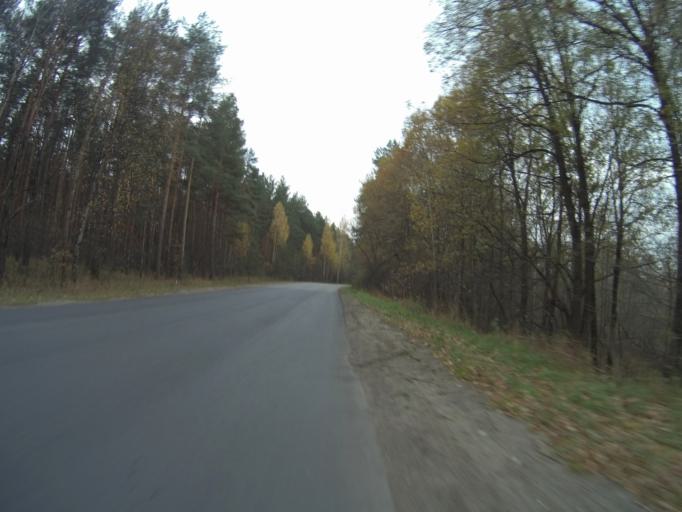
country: RU
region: Vladimir
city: Kommunar
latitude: 56.1273
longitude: 40.4826
